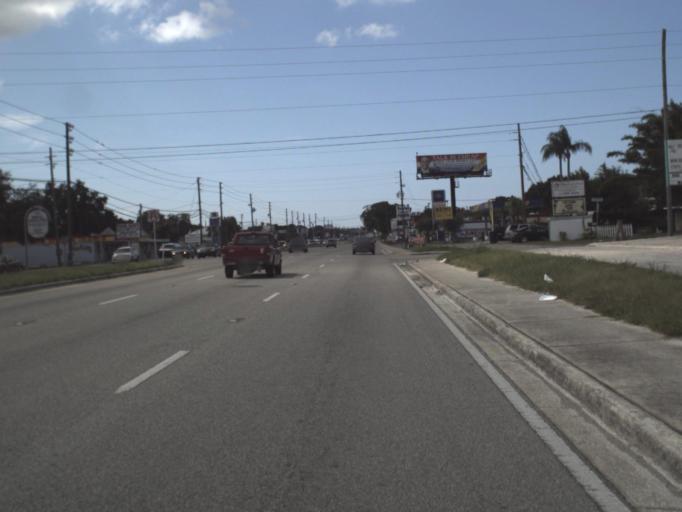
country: US
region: Florida
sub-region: Pinellas County
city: Seminole
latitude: 27.8700
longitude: -82.7872
